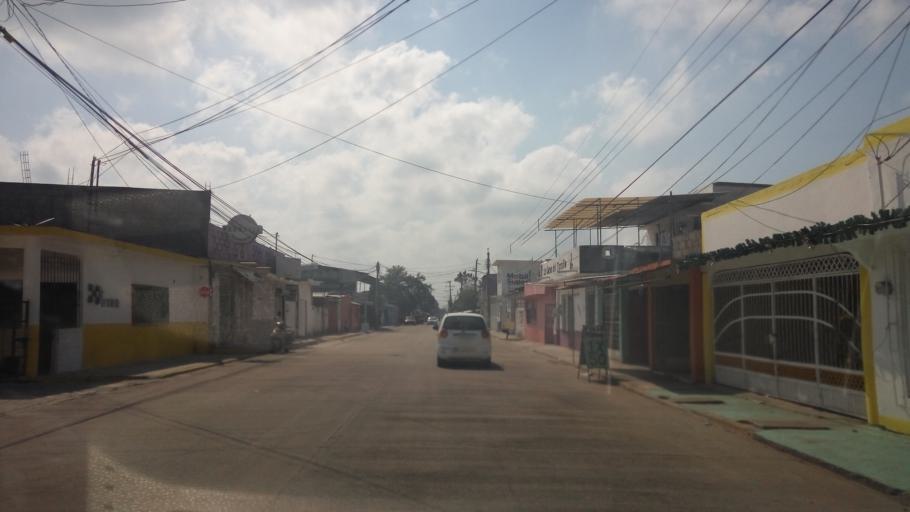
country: MX
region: Tabasco
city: Frontera
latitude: 18.5292
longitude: -92.6388
